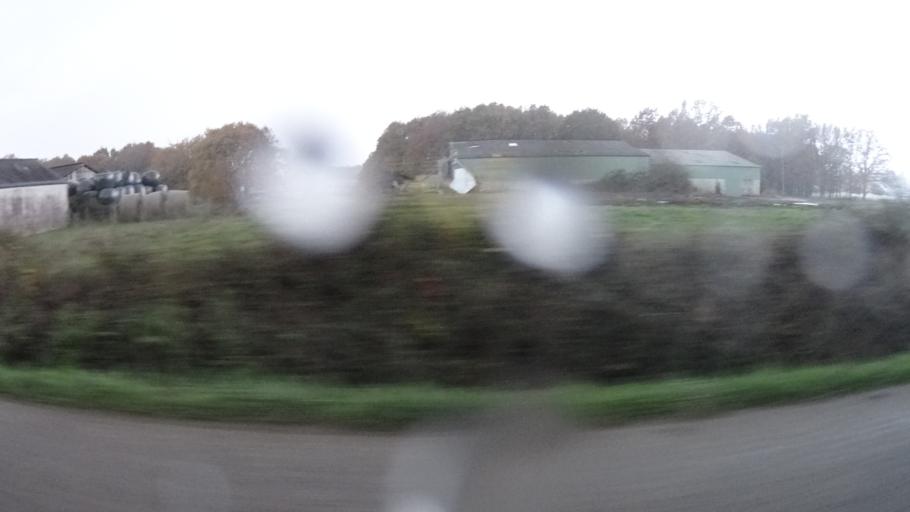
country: FR
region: Pays de la Loire
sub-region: Departement de la Loire-Atlantique
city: Avessac
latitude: 47.6626
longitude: -1.9872
